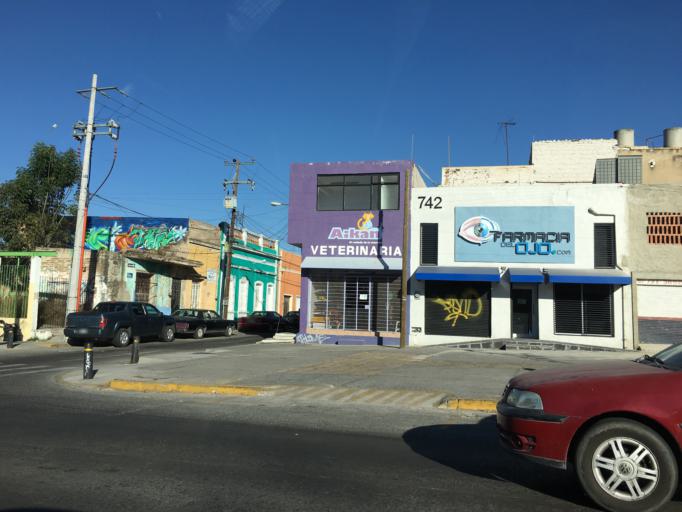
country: MX
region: Jalisco
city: Guadalajara
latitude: 20.6878
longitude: -103.3538
